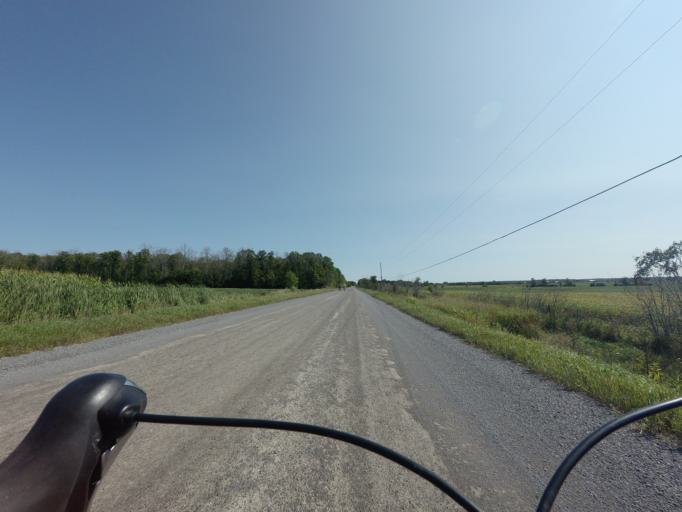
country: CA
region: Ontario
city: Arnprior
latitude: 45.3965
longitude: -76.1715
